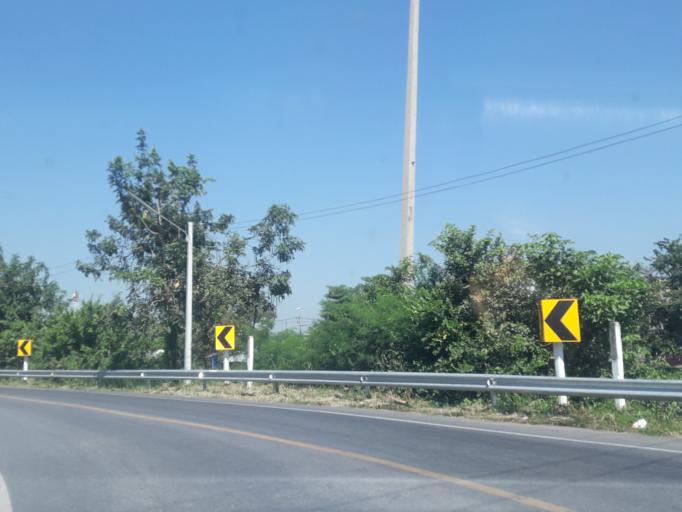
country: TH
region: Sara Buri
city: Nong Khae
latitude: 14.3330
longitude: 100.8735
